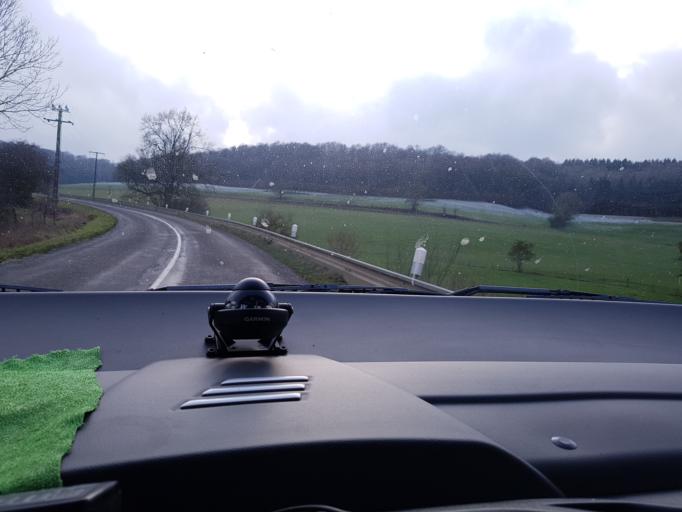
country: FR
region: Champagne-Ardenne
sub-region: Departement des Ardennes
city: Rimogne
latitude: 49.7731
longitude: 4.4476
